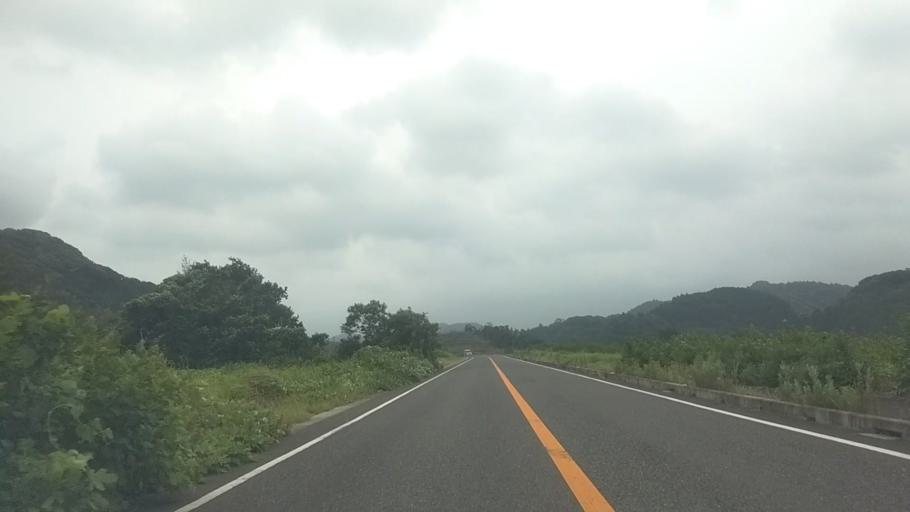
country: JP
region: Chiba
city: Kimitsu
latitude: 35.2195
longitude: 139.9392
